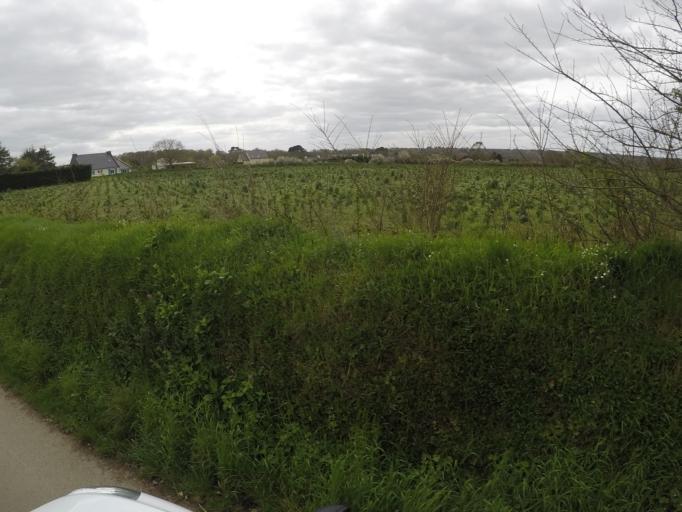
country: FR
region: Brittany
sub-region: Departement des Cotes-d'Armor
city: Plouezec
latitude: 48.7166
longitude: -2.9582
